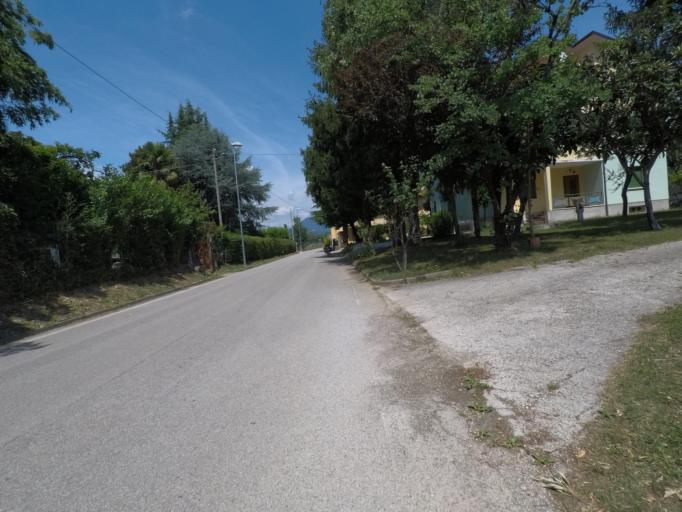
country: IT
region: Friuli Venezia Giulia
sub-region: Provincia di Pordenone
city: Spilimbergo
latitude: 46.1333
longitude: 12.9034
